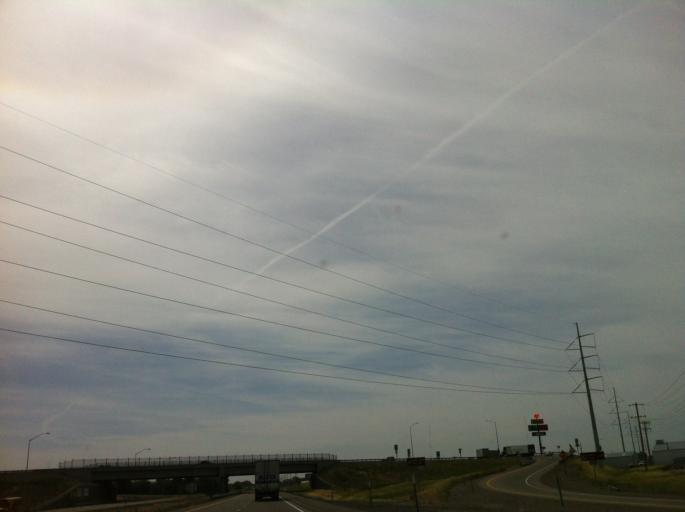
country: US
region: Oregon
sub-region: Malheur County
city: Ontario
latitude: 44.0525
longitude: -116.9816
